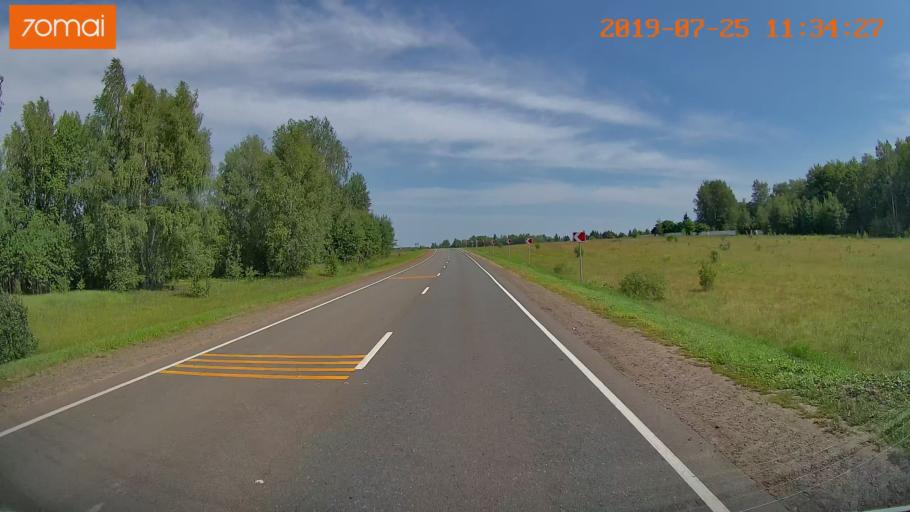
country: RU
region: Ivanovo
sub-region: Privolzhskiy Rayon
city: Ples
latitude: 57.3997
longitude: 41.4130
